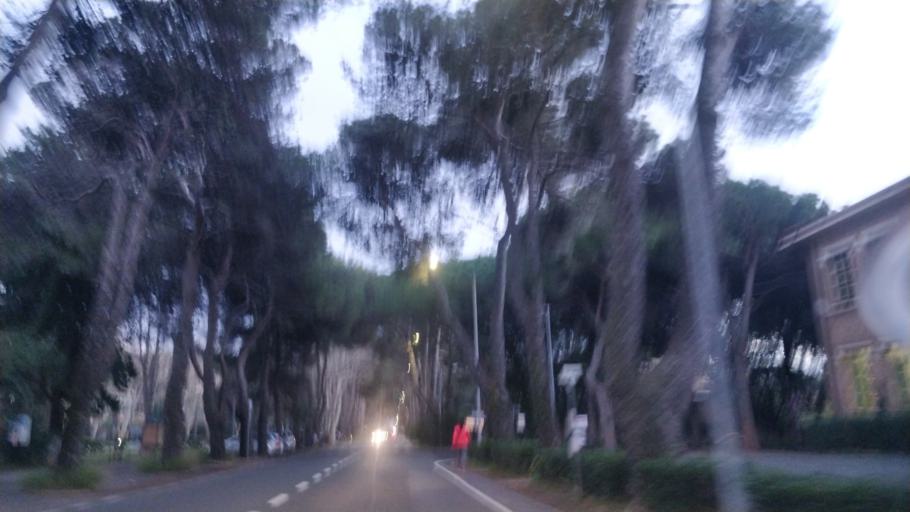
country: IT
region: Tuscany
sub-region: Provincia di Livorno
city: Rosignano Solvay-Castiglioncello
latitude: 43.3910
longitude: 10.4402
